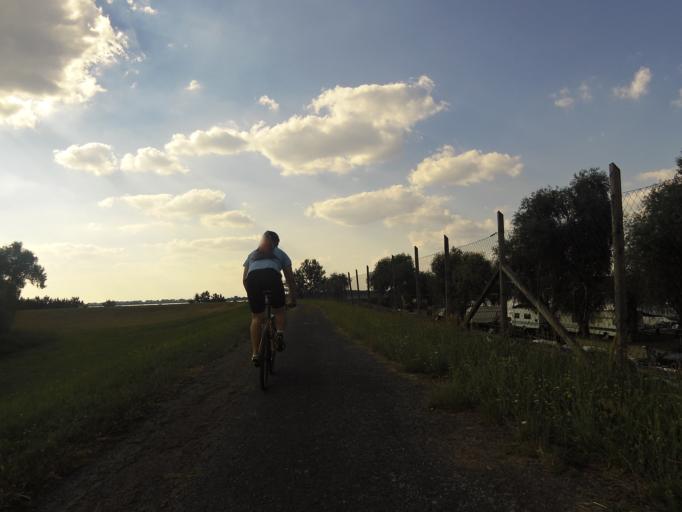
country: HU
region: Jasz-Nagykun-Szolnok
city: Abadszalok
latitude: 47.4876
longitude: 20.6037
